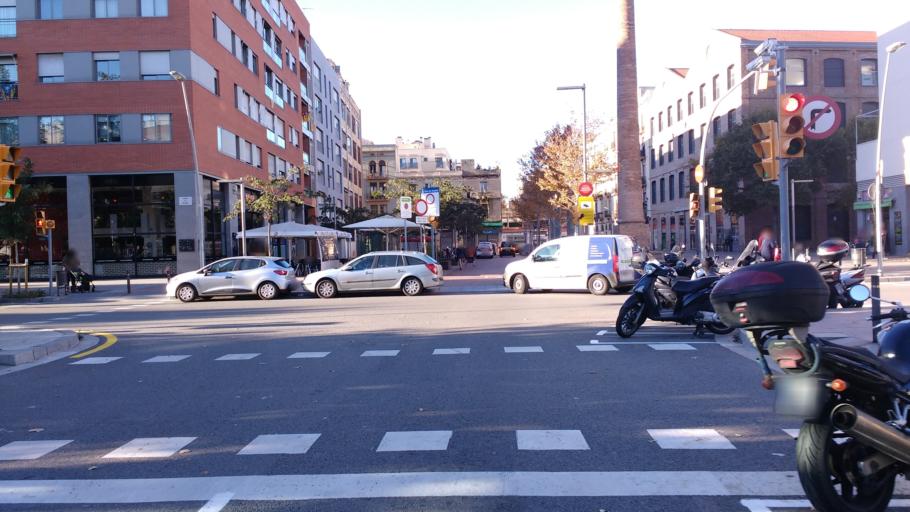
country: ES
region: Catalonia
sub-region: Provincia de Barcelona
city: Sant Marti
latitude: 41.4018
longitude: 2.2055
